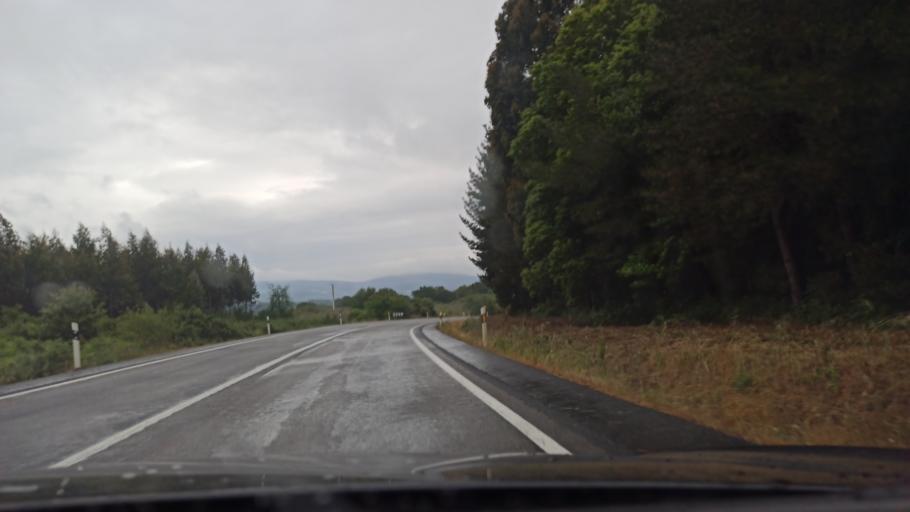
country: ES
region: Galicia
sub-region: Provincia de Lugo
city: Monterroso
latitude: 42.8026
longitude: -7.7859
